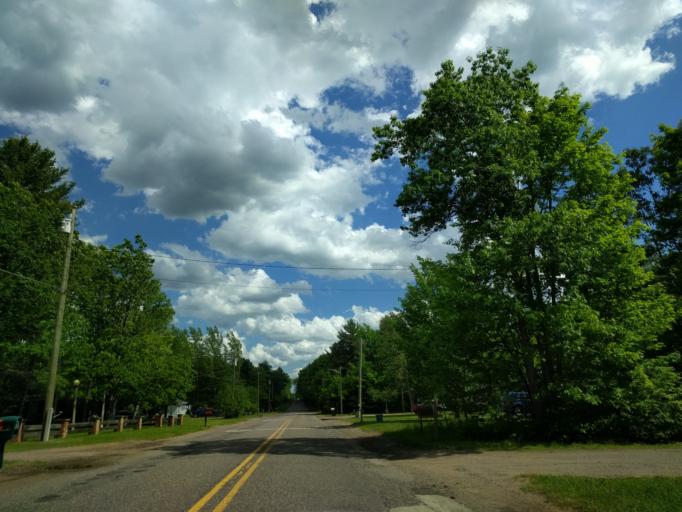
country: US
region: Michigan
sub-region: Marquette County
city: Trowbridge Park
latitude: 46.5468
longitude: -87.5200
